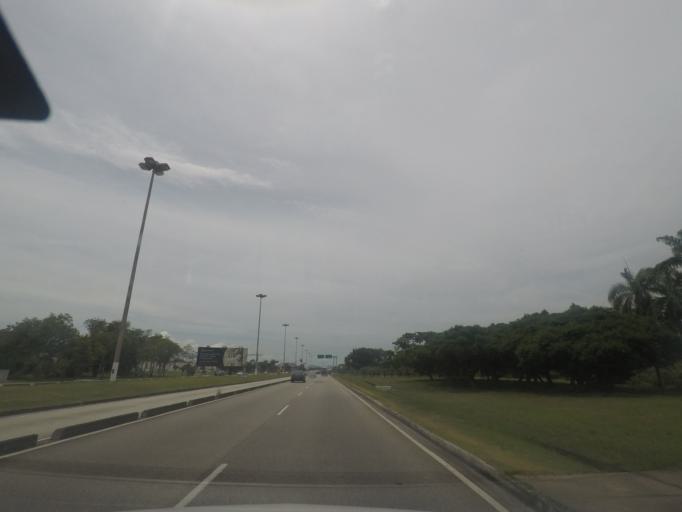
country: BR
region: Rio de Janeiro
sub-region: Duque De Caxias
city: Duque de Caxias
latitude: -22.8189
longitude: -43.2371
